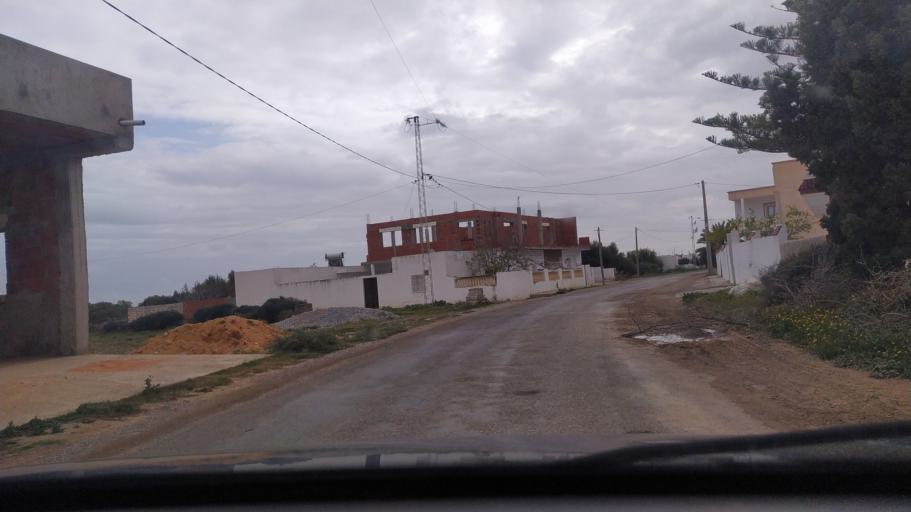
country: TN
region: Al Munastir
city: Sidi Bin Nur
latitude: 35.5144
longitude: 10.9664
